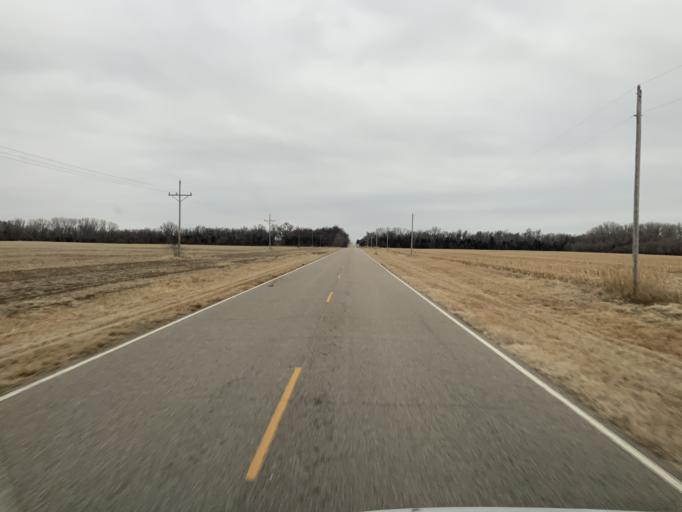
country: US
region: Kansas
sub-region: Reno County
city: South Hutchinson
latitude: 37.9390
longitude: -98.0869
